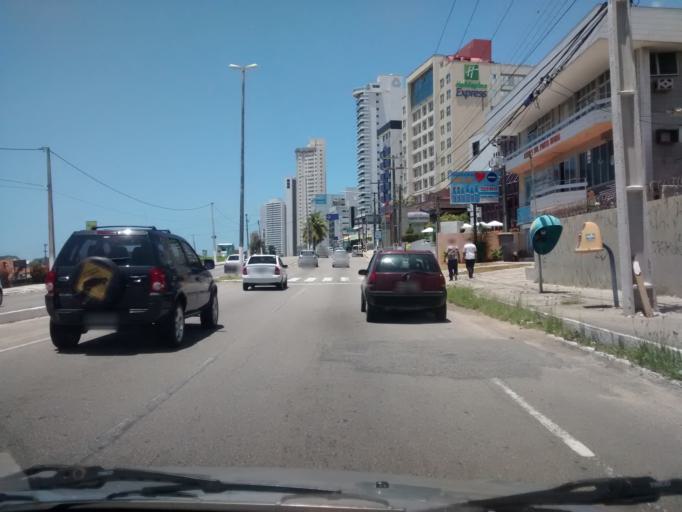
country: BR
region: Rio Grande do Norte
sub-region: Natal
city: Natal
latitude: -5.8716
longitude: -35.1807
